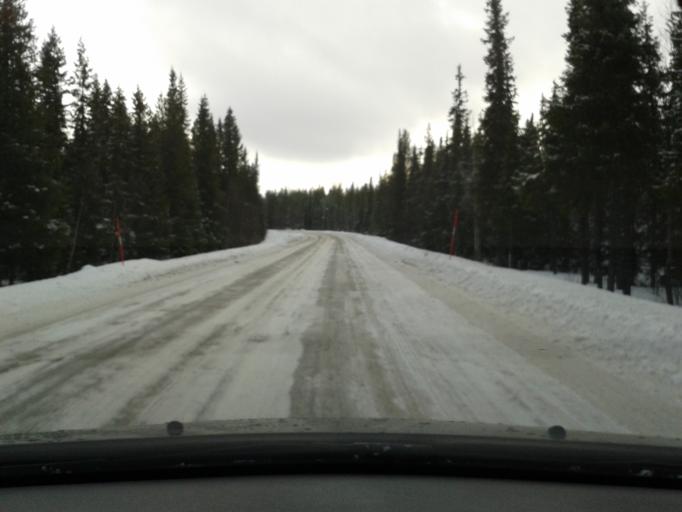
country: SE
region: Vaesterbotten
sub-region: Vilhelmina Kommun
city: Sjoberg
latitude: 64.7592
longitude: 16.1568
